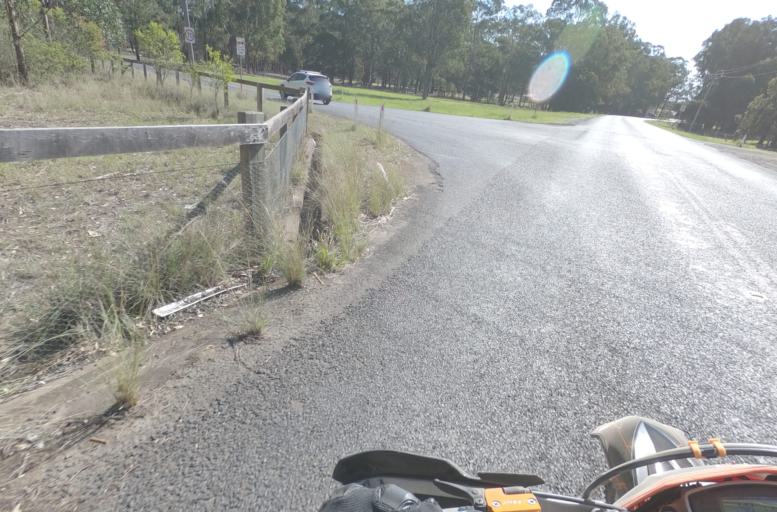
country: AU
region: New South Wales
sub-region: Hawkesbury
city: Pitt Town
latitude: -33.5812
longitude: 150.8778
